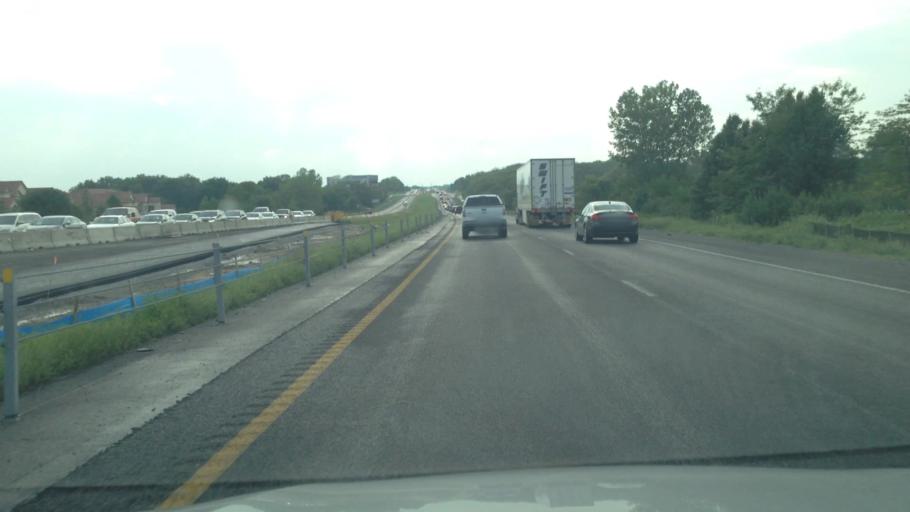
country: US
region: Missouri
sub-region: Clay County
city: Pleasant Valley
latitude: 39.2451
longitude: -94.4782
